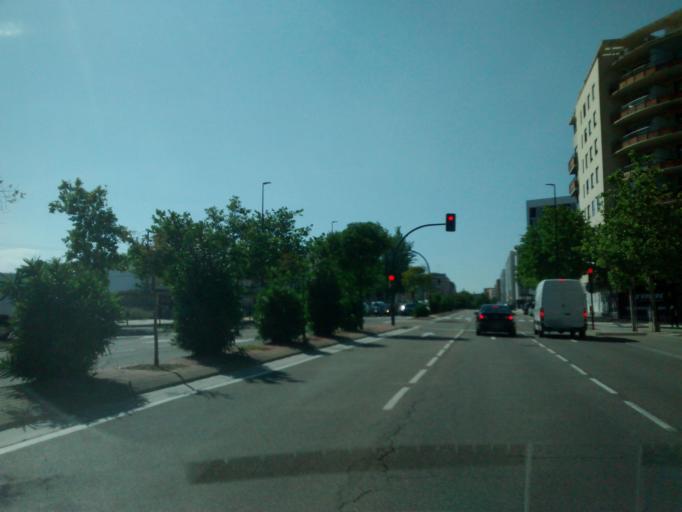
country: ES
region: Aragon
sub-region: Provincia de Zaragoza
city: Zaragoza
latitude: 41.6349
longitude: -0.8634
